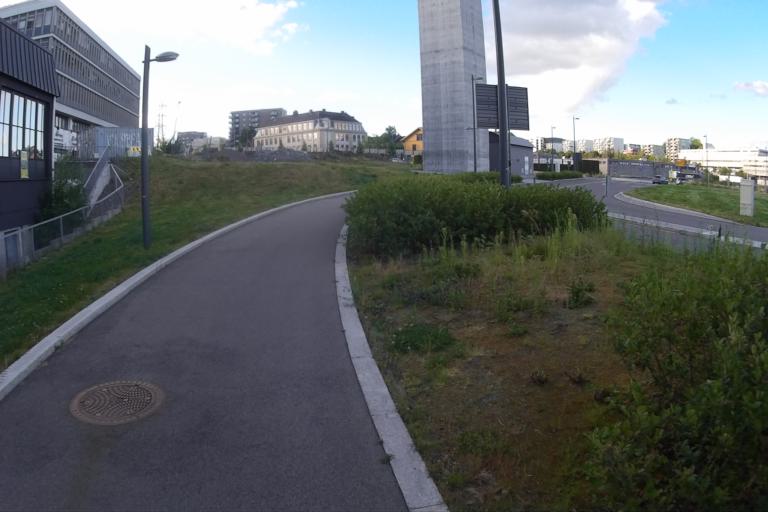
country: NO
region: Oslo
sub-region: Oslo
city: Oslo
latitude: 59.9300
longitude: 10.8018
